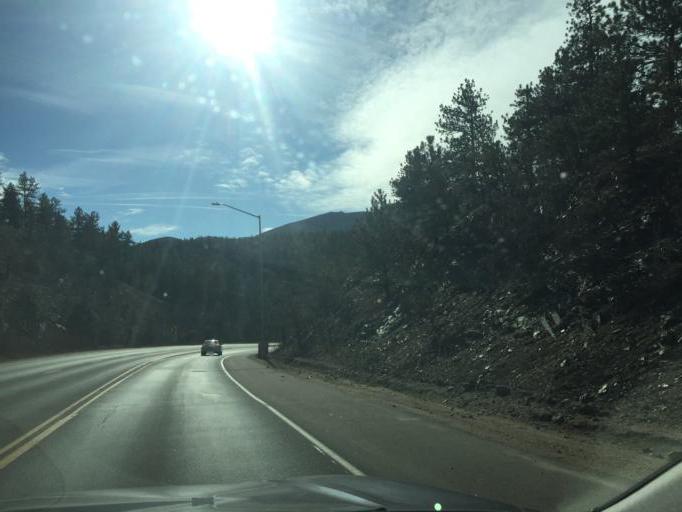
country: US
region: Colorado
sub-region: Jefferson County
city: Evergreen
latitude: 39.4084
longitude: -105.4733
